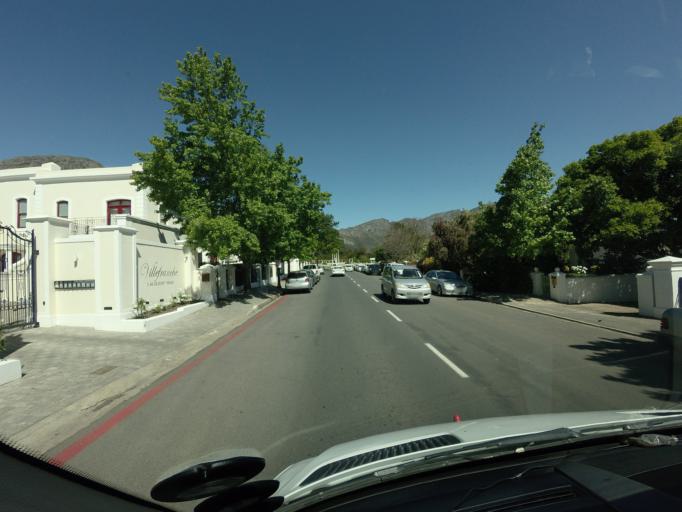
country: ZA
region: Western Cape
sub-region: Cape Winelands District Municipality
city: Paarl
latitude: -33.9134
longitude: 19.1219
